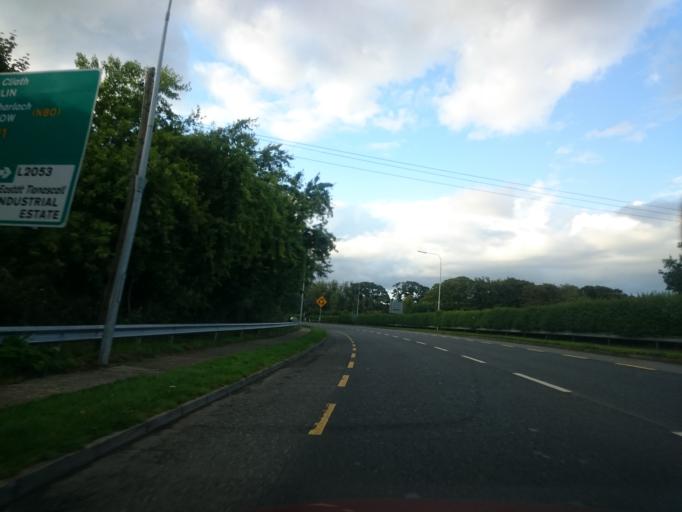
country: IE
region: Leinster
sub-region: Loch Garman
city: Enniscorthy
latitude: 52.5114
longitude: -6.5644
